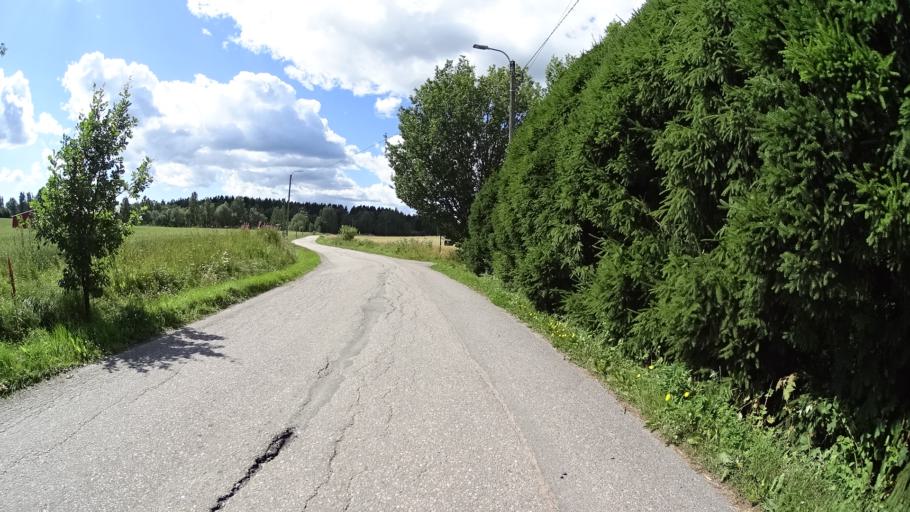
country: FI
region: Uusimaa
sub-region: Helsinki
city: Teekkarikylae
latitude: 60.2960
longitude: 24.8785
